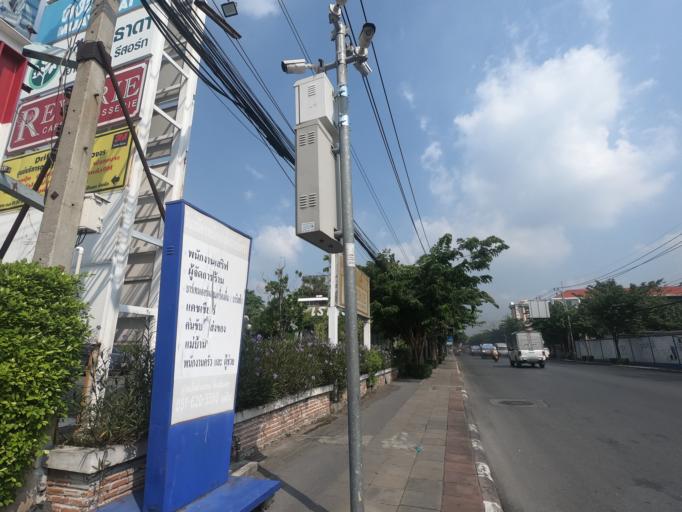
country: TH
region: Bangkok
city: Lat Phrao
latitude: 13.8218
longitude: 100.6088
